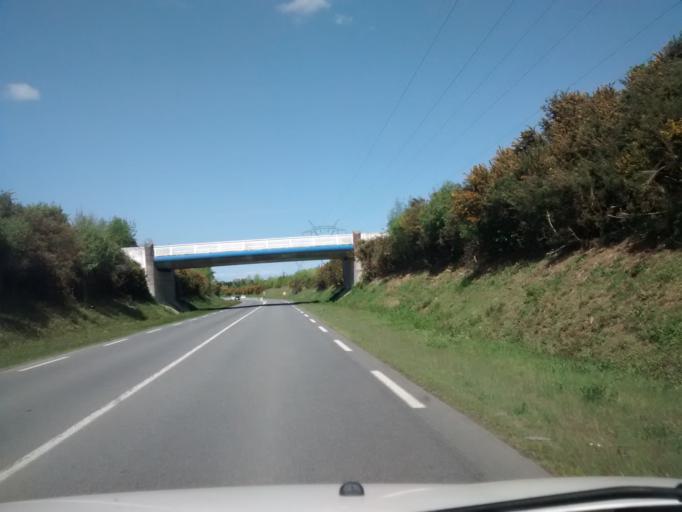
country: FR
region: Brittany
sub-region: Departement des Cotes-d'Armor
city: Pleslin-Trigavou
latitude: 48.5331
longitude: -2.0370
